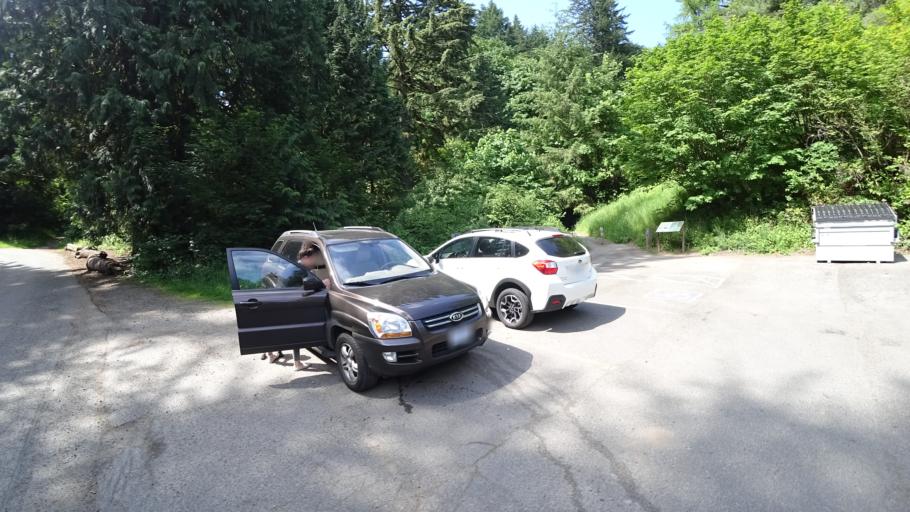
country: US
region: Oregon
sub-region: Multnomah County
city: Portland
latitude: 45.5163
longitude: -122.7190
